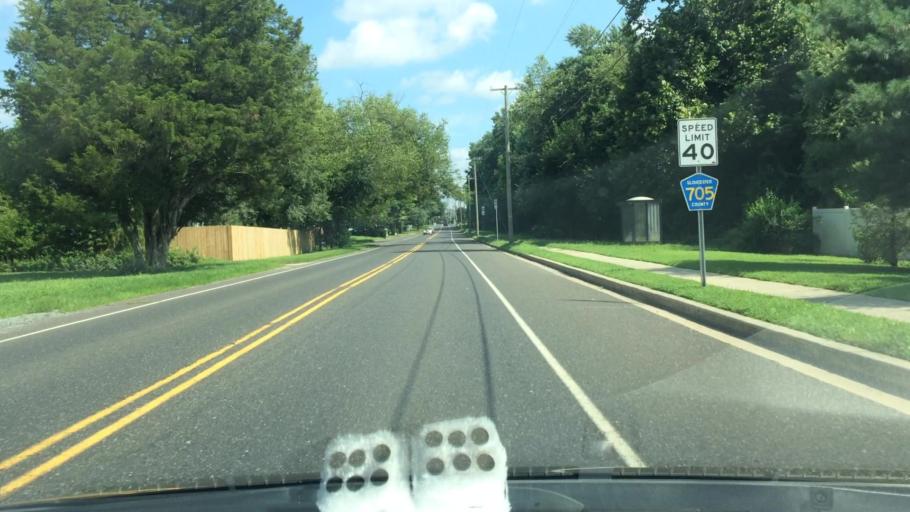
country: US
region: New Jersey
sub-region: Gloucester County
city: Turnersville
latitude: 39.7818
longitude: -75.0652
